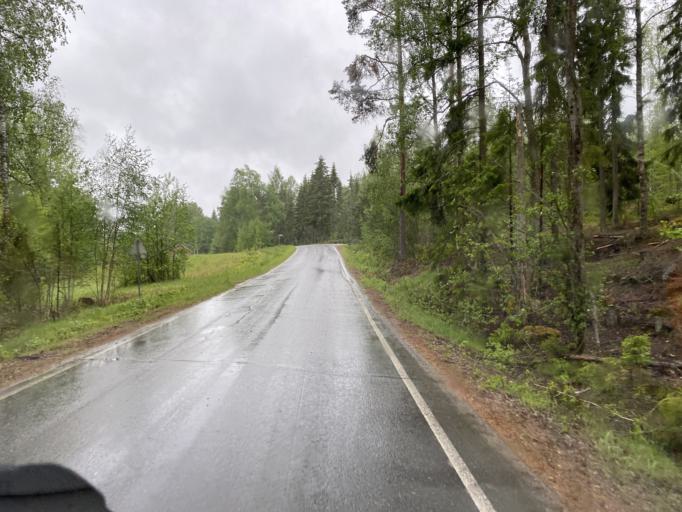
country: FI
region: Haeme
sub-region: Forssa
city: Humppila
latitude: 61.0733
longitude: 23.3119
